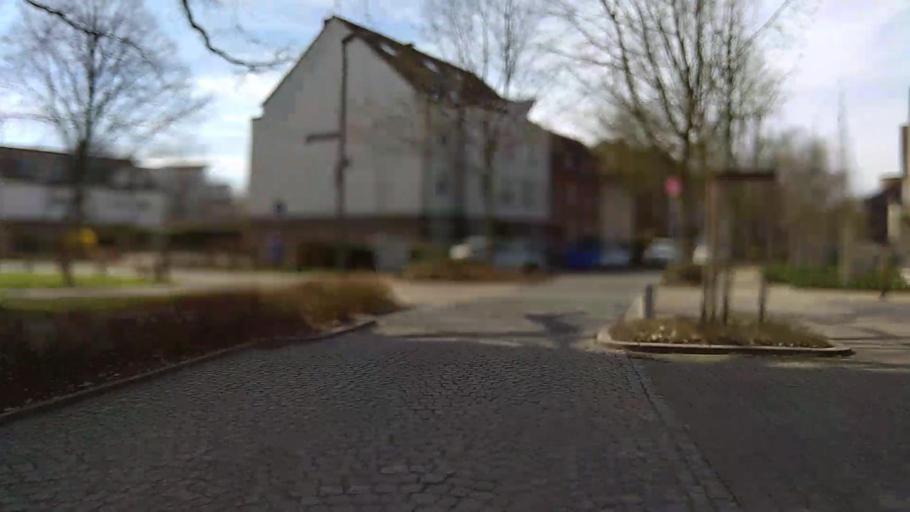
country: DE
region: North Rhine-Westphalia
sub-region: Regierungsbezirk Munster
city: Gladbeck
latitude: 51.5823
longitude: 7.0632
